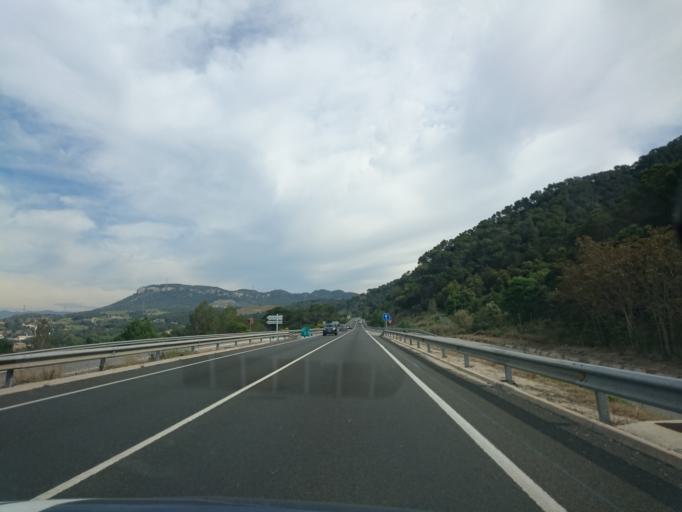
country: ES
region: Catalonia
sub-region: Provincia de Barcelona
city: Capellades
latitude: 41.5428
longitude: 1.6917
